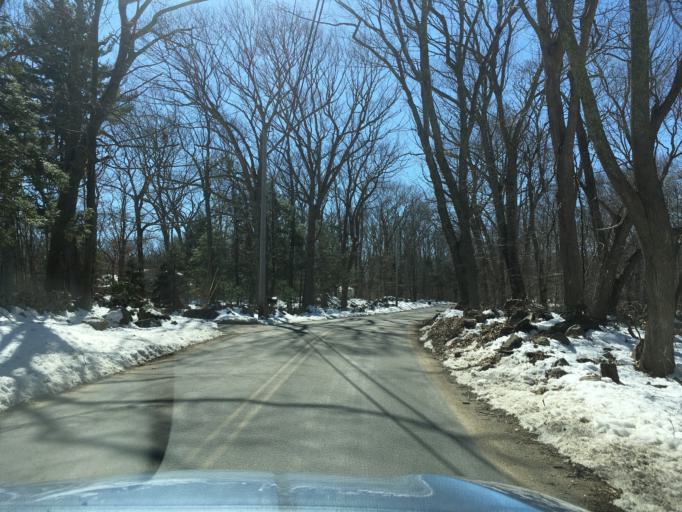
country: US
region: Rhode Island
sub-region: Washington County
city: Exeter
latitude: 41.6067
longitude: -71.5174
